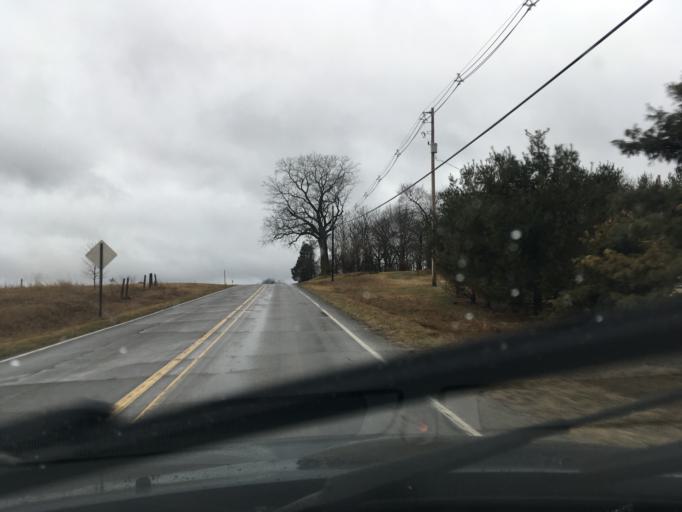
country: US
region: Michigan
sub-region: Jackson County
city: Grass Lake
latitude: 42.3101
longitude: -84.1336
